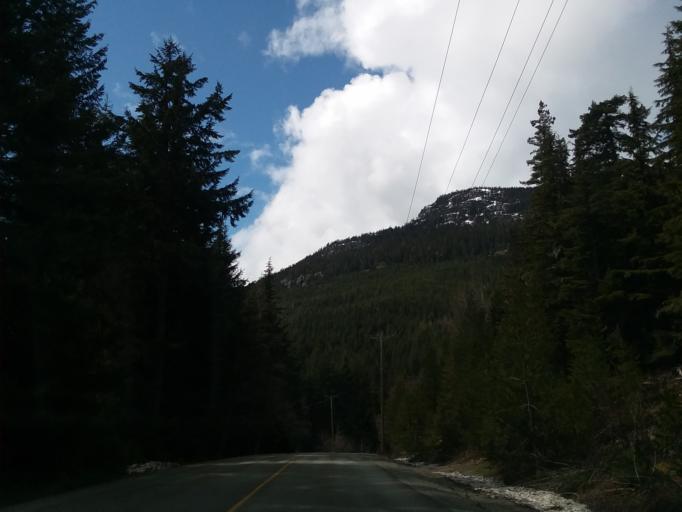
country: CA
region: British Columbia
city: Whistler
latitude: 50.1309
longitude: -122.9824
